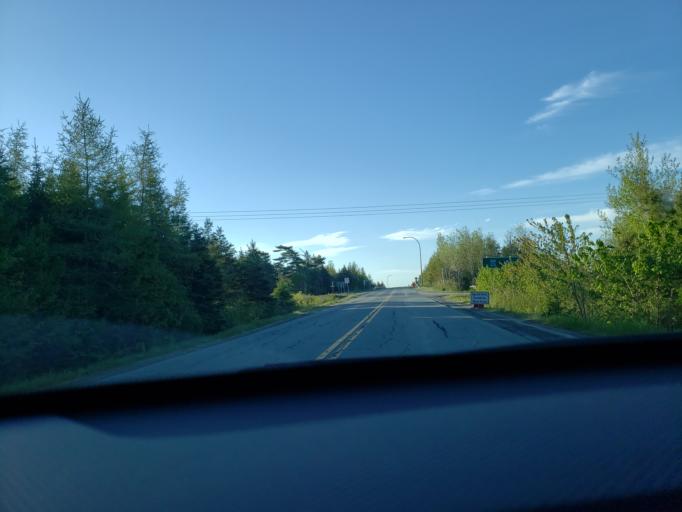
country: CA
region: Nova Scotia
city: Cole Harbour
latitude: 44.7145
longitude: -63.3960
